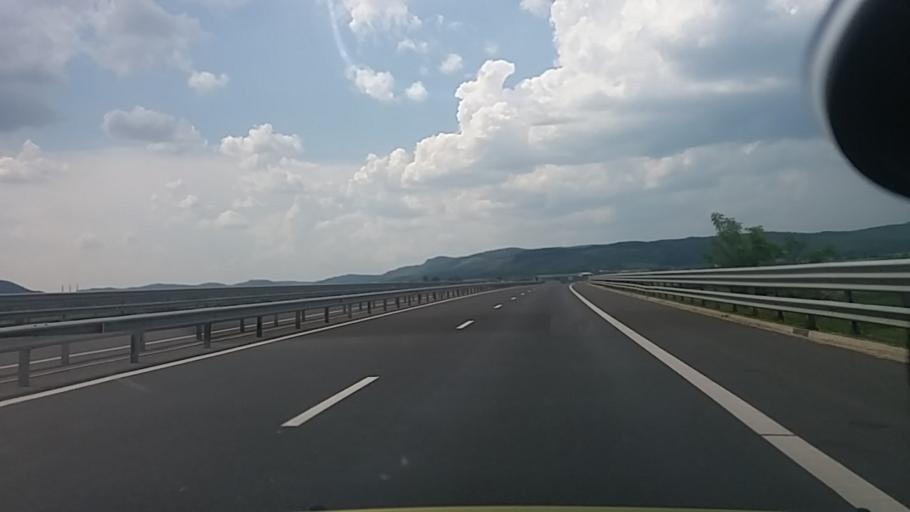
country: RO
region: Hunedoara
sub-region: Comuna Harau
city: Harau
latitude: 45.9004
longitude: 22.9317
